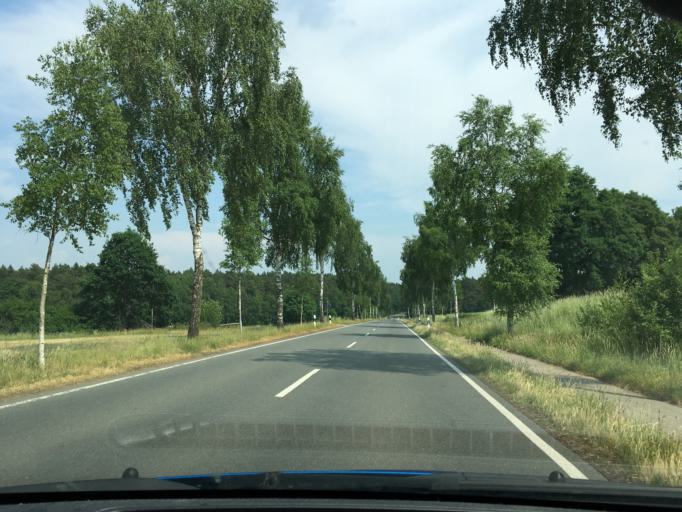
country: DE
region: Lower Saxony
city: Jesteburg
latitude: 53.2710
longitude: 9.9398
